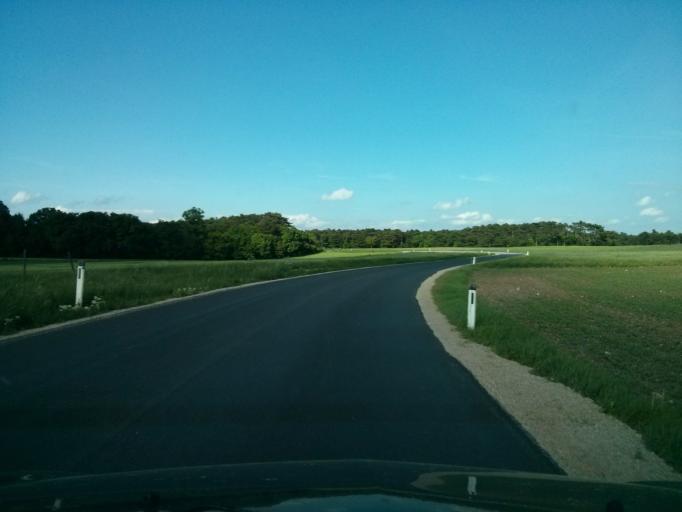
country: AT
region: Lower Austria
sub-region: Politischer Bezirk Baden
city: Hernstein
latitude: 47.9042
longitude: 16.1274
